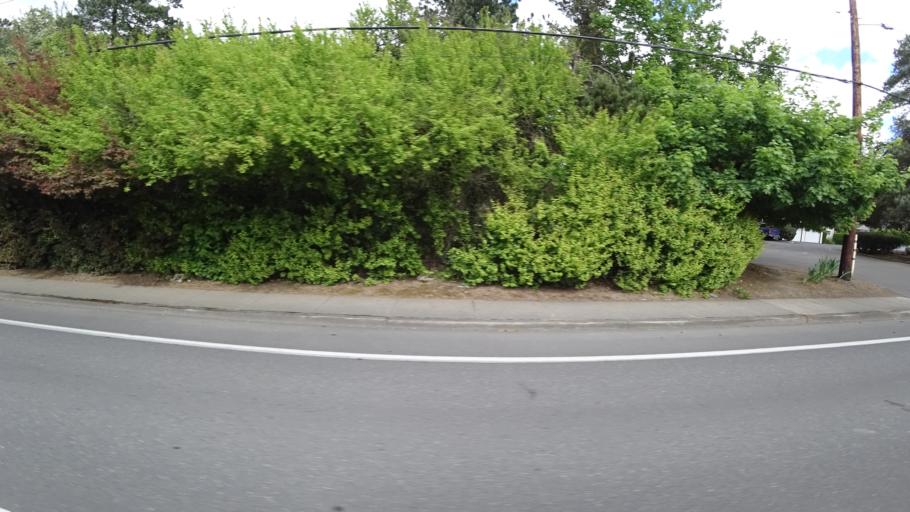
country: US
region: Oregon
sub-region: Washington County
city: Beaverton
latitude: 45.4805
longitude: -122.8261
